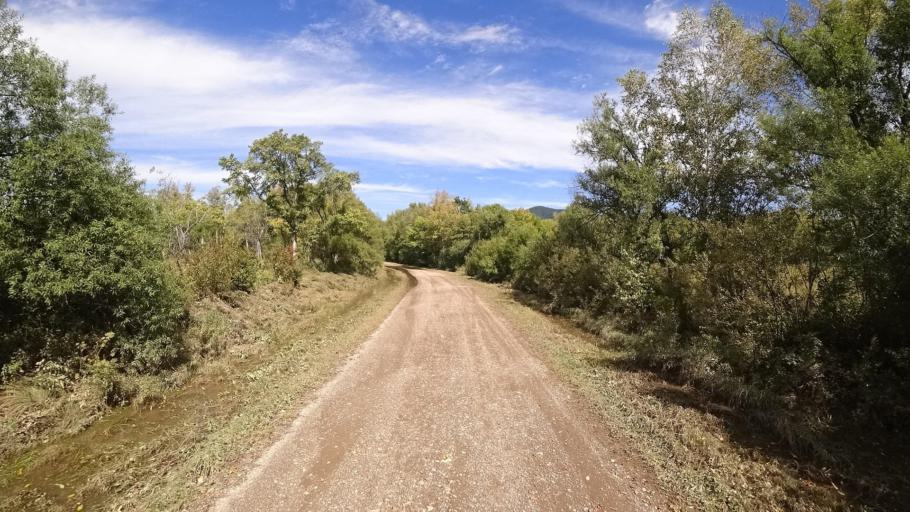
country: RU
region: Primorskiy
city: Yakovlevka
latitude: 44.6622
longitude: 133.7502
